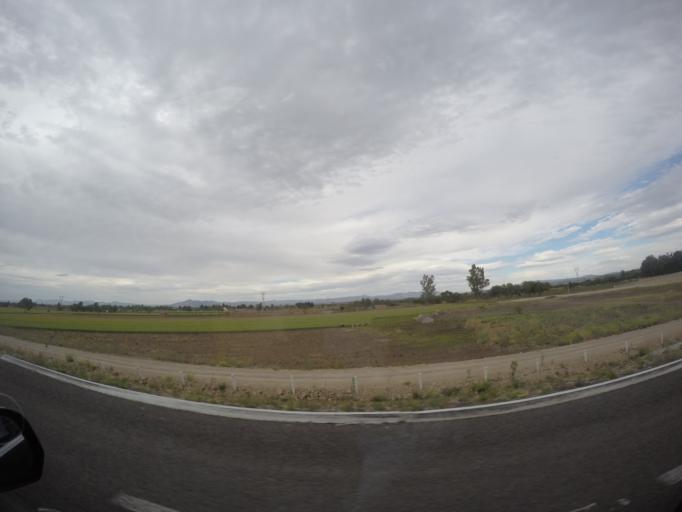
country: MX
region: Guanajuato
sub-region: Irapuato
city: Serrano
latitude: 20.8006
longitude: -101.4295
